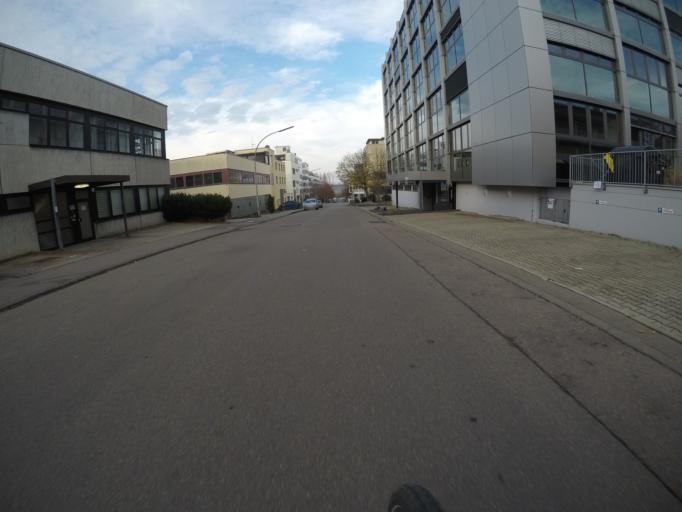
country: DE
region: Baden-Wuerttemberg
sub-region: Regierungsbezirk Stuttgart
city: Leinfelden-Echterdingen
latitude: 48.6952
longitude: 9.1633
